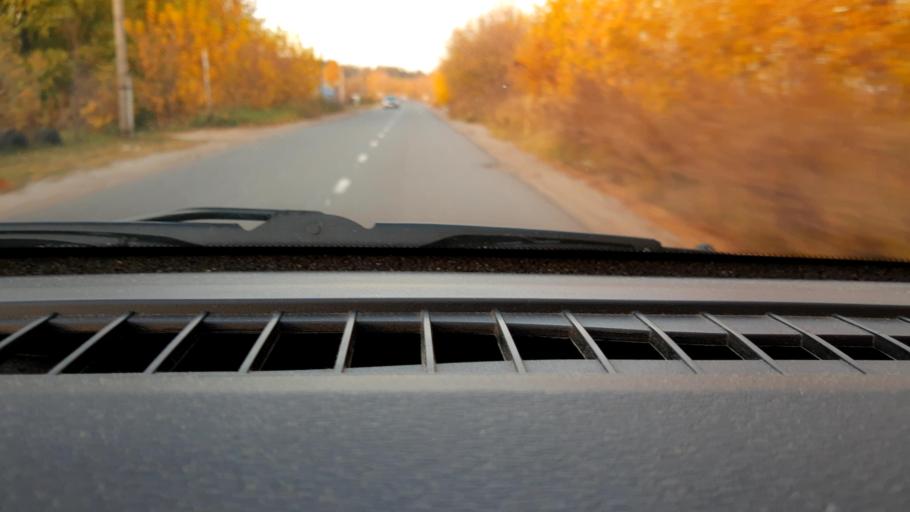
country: RU
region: Nizjnij Novgorod
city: Kstovo
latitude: 56.1858
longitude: 44.1517
